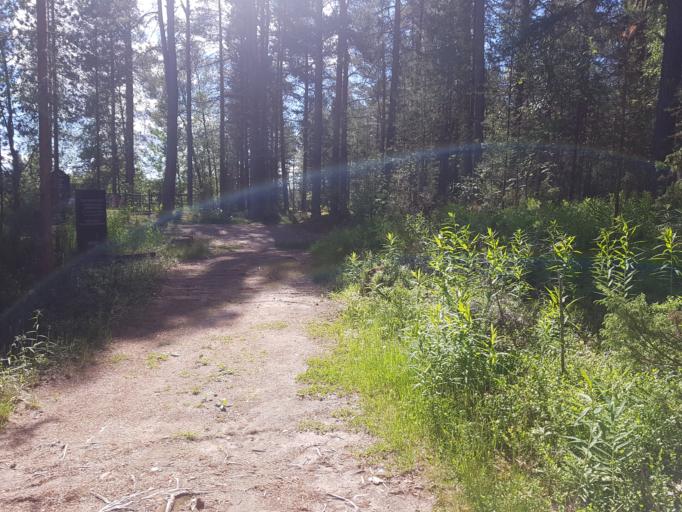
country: RU
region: Republic of Karelia
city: Yushkozero
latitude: 64.7433
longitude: 32.0981
